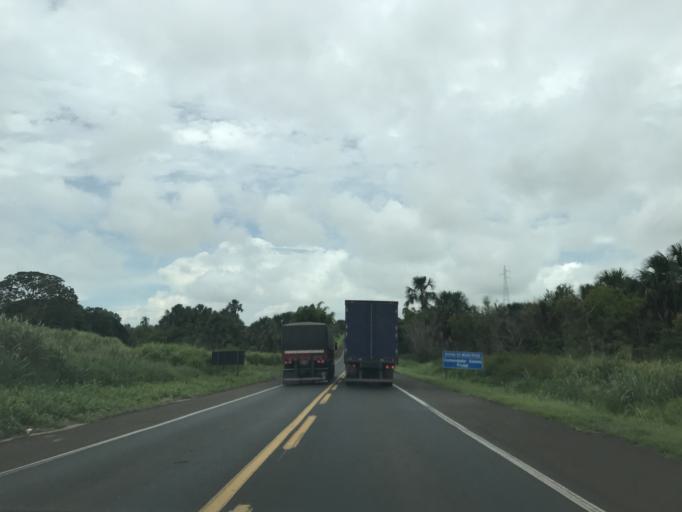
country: BR
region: Minas Gerais
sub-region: Frutal
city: Frutal
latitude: -19.7954
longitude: -48.9669
